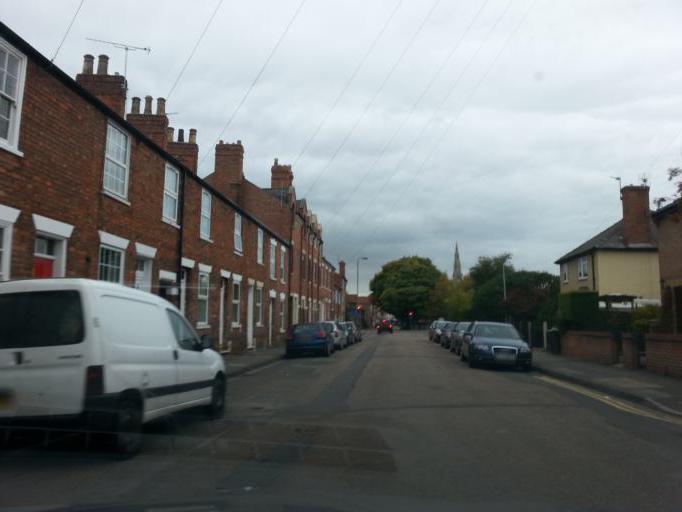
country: GB
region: England
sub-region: Nottinghamshire
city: Newark on Trent
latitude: 53.0745
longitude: -0.8027
